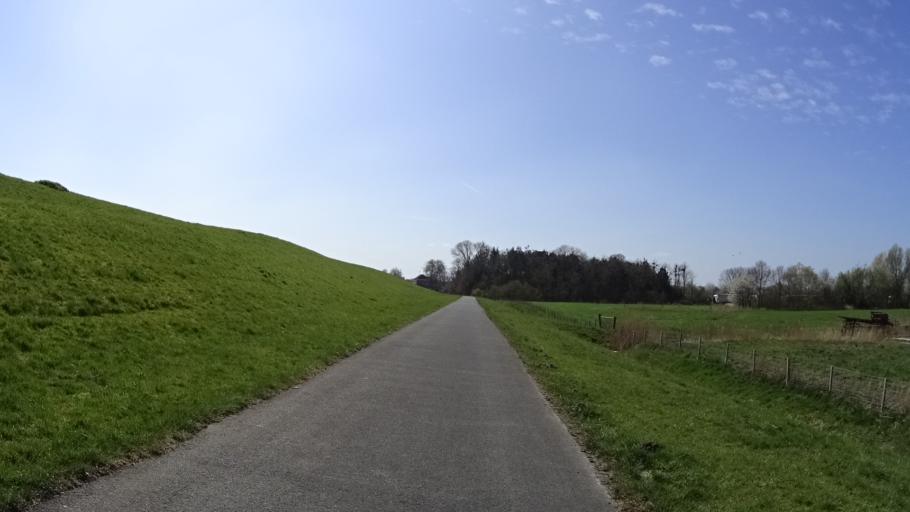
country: DE
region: Lower Saxony
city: Weener
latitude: 53.1737
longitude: 7.3706
